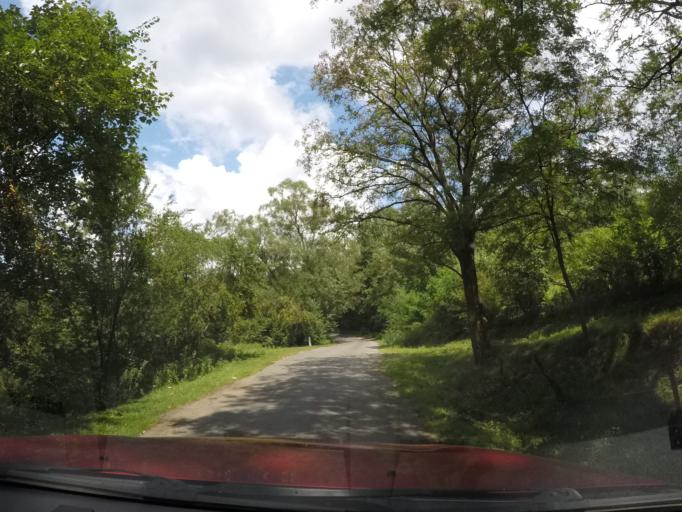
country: UA
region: Zakarpattia
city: Velykyi Bereznyi
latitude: 49.0102
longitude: 22.6306
